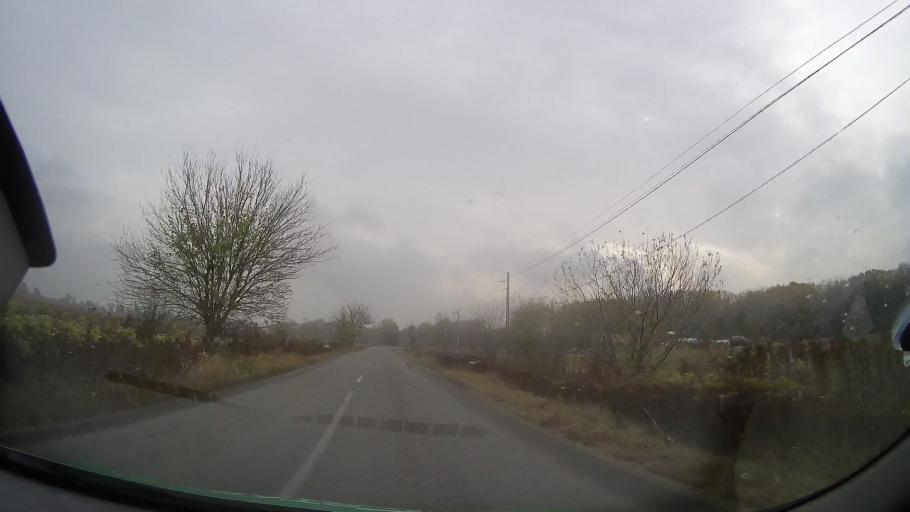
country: RO
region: Prahova
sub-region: Comuna Gherghita
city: Gherghita
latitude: 44.8146
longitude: 26.2682
